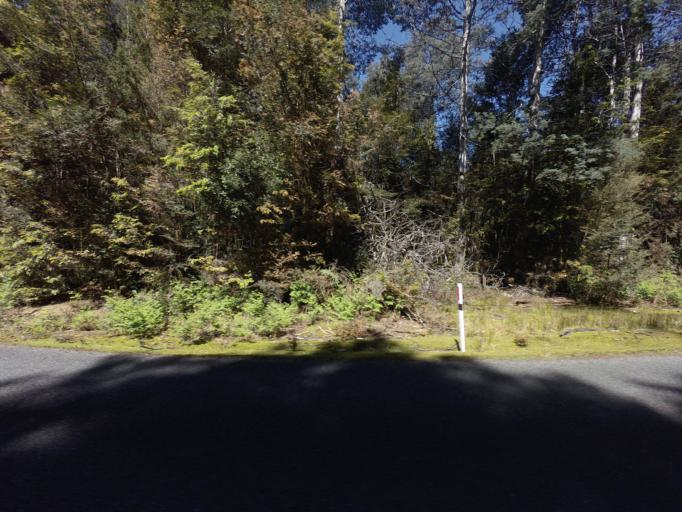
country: AU
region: Tasmania
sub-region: Huon Valley
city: Geeveston
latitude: -42.8154
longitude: 146.3679
